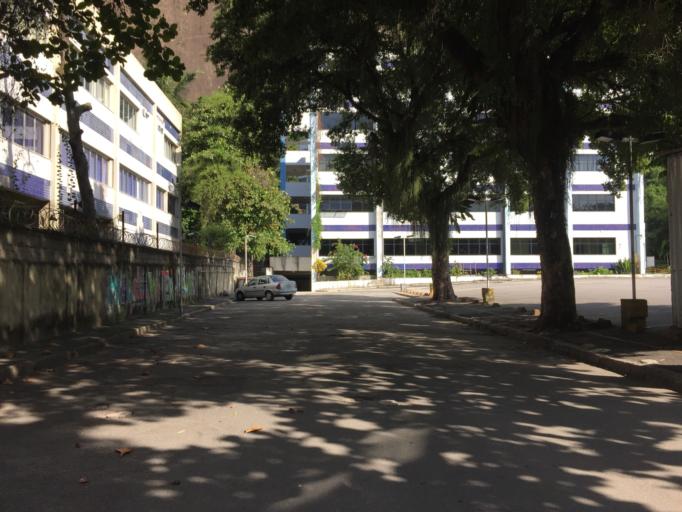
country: BR
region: Rio de Janeiro
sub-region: Rio De Janeiro
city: Rio de Janeiro
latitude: -22.9544
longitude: -43.1684
